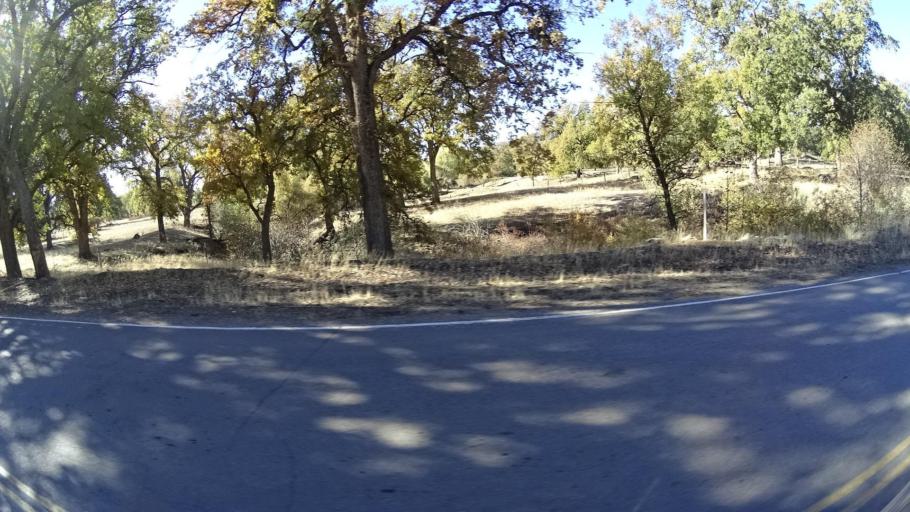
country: US
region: California
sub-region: Kern County
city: Alta Sierra
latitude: 35.7865
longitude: -118.7045
